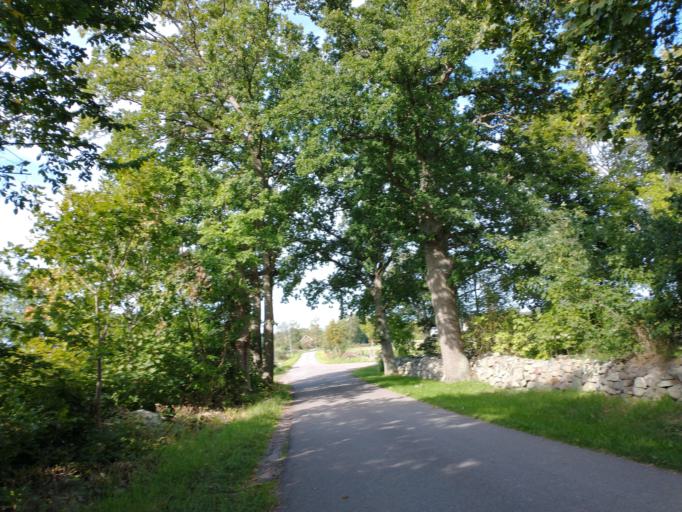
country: SE
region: Kalmar
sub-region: Kalmar Kommun
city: Lindsdal
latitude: 56.7774
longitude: 16.3127
